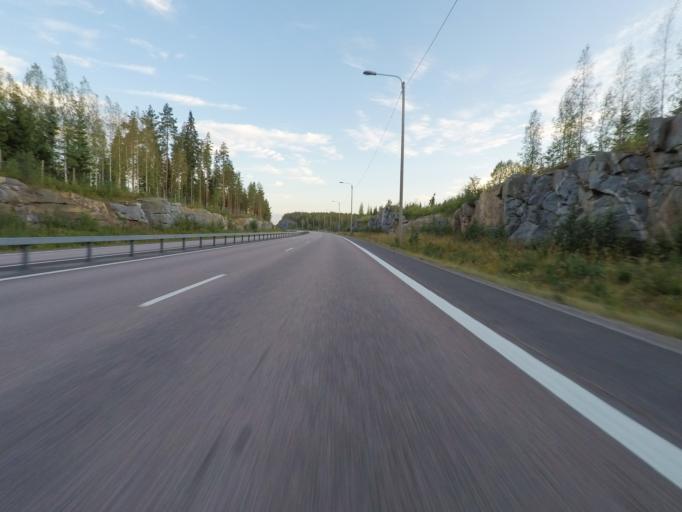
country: FI
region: Central Finland
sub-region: Jyvaeskylae
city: Saeynaetsalo
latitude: 62.2142
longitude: 25.8904
